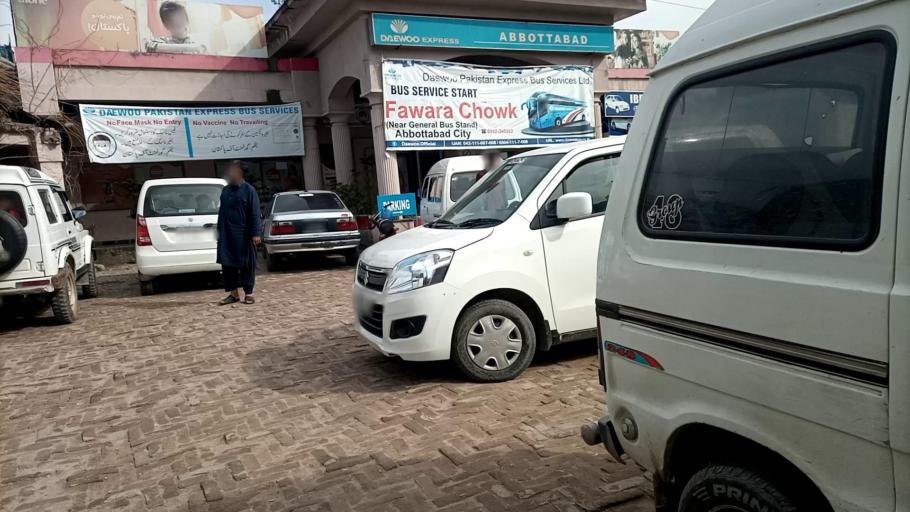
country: PK
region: Khyber Pakhtunkhwa
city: Abbottabad
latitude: 34.1926
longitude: 73.2351
